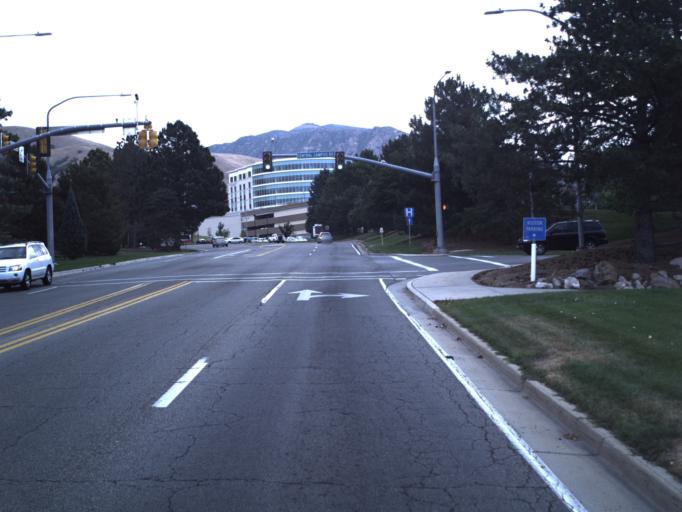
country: US
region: Utah
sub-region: Salt Lake County
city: Salt Lake City
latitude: 40.7709
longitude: -111.8455
